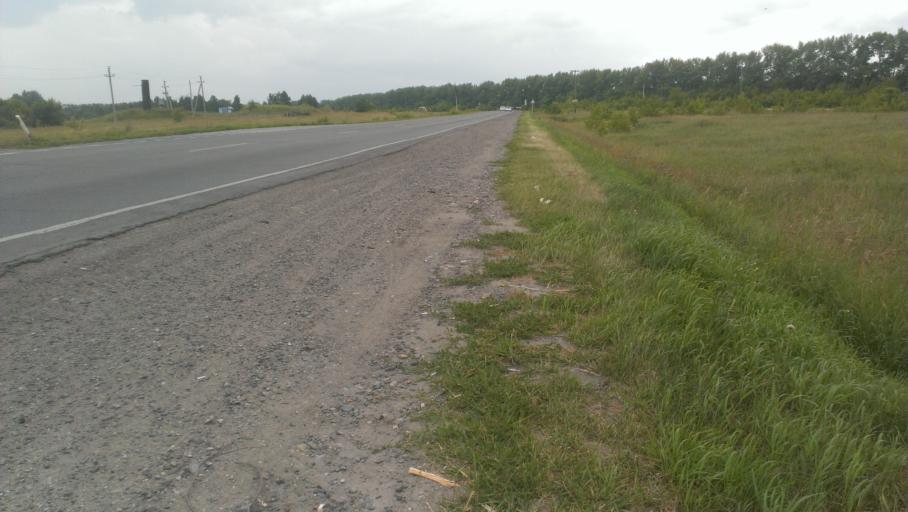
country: RU
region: Altai Krai
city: Gon'ba
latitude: 53.3892
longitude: 83.6016
